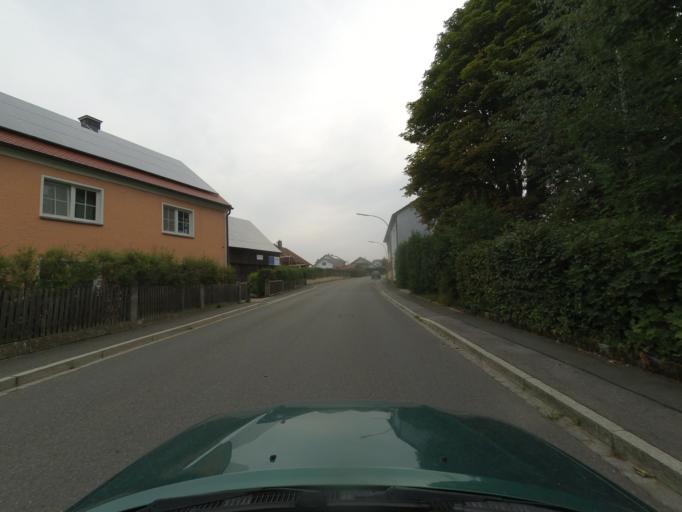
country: DE
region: Bavaria
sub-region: Upper Palatinate
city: Eslarn
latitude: 49.5804
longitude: 12.5251
